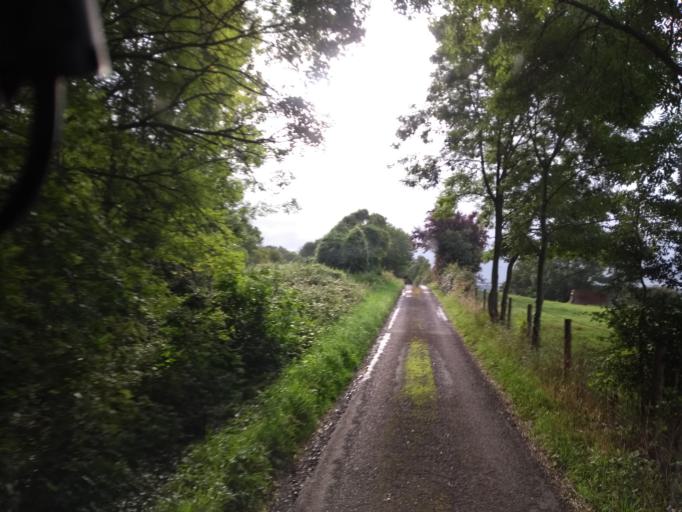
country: GB
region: England
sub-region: Somerset
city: Castle Cary
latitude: 51.0275
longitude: -2.5835
